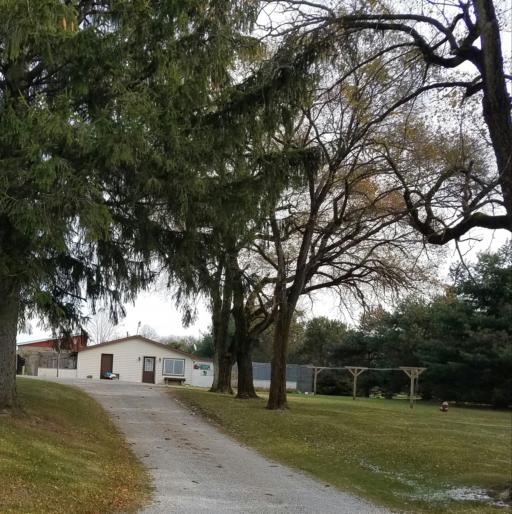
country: US
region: Ohio
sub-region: Morrow County
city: Mount Gilead
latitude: 40.5496
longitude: -82.7353
